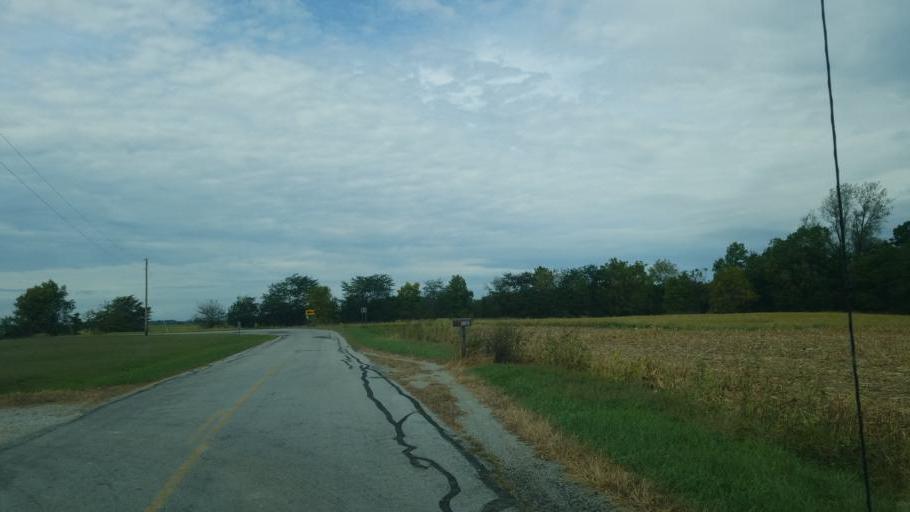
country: US
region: Ohio
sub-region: Hardin County
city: Forest
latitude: 40.6862
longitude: -83.4201
